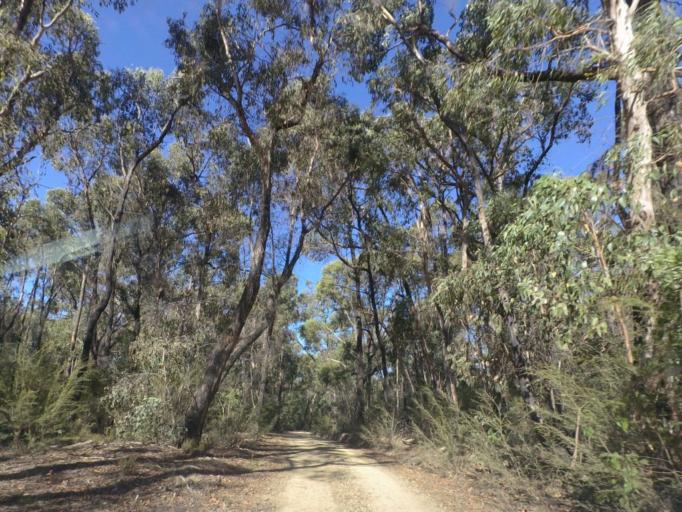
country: AU
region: Victoria
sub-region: Murrindindi
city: Kinglake West
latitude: -37.4628
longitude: 145.3783
